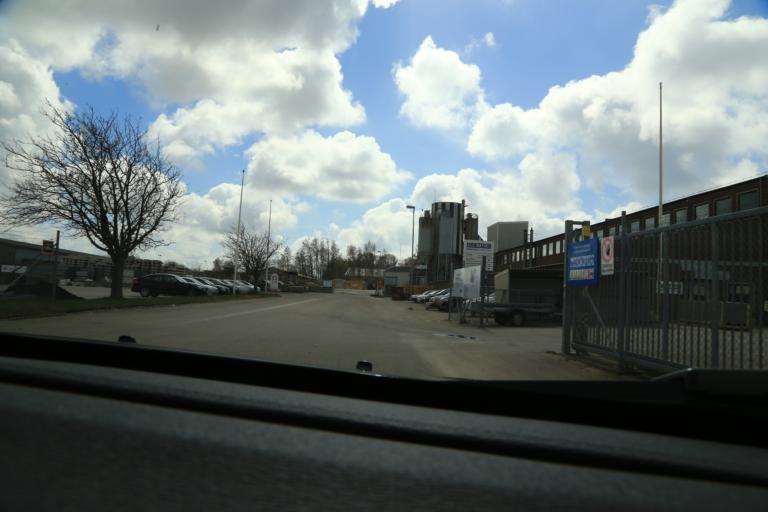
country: SE
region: Halland
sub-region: Varbergs Kommun
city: Varberg
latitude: 57.1216
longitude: 12.2826
